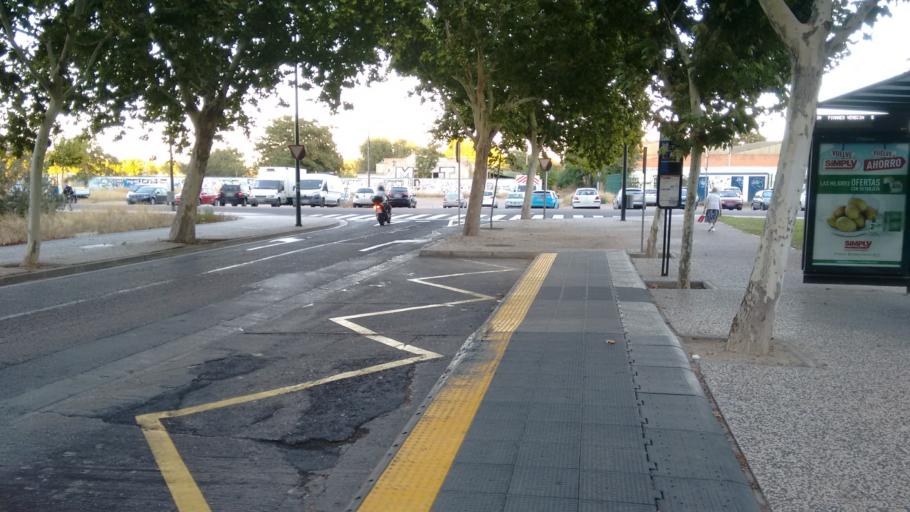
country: ES
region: Aragon
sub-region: Provincia de Zaragoza
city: Zaragoza
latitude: 41.6550
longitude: -0.8560
